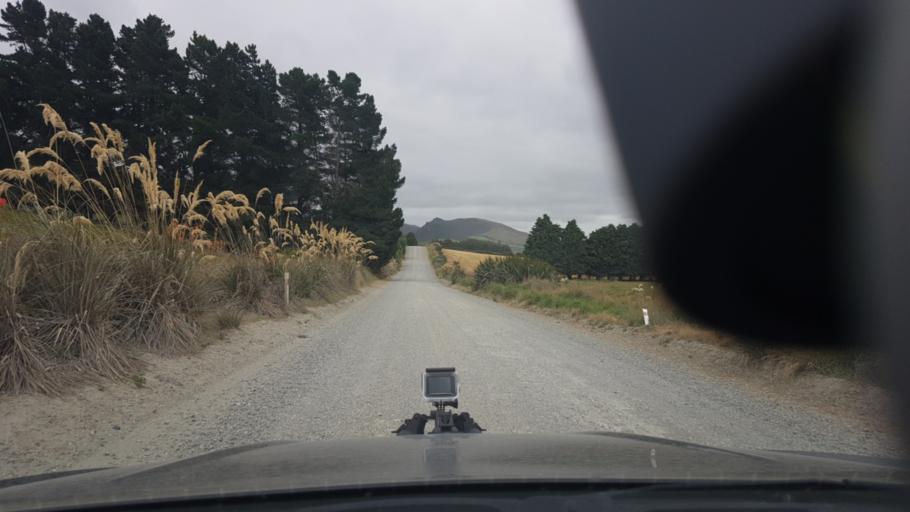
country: NZ
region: Otago
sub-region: Clutha District
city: Papatowai
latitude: -46.3451
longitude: 169.4404
